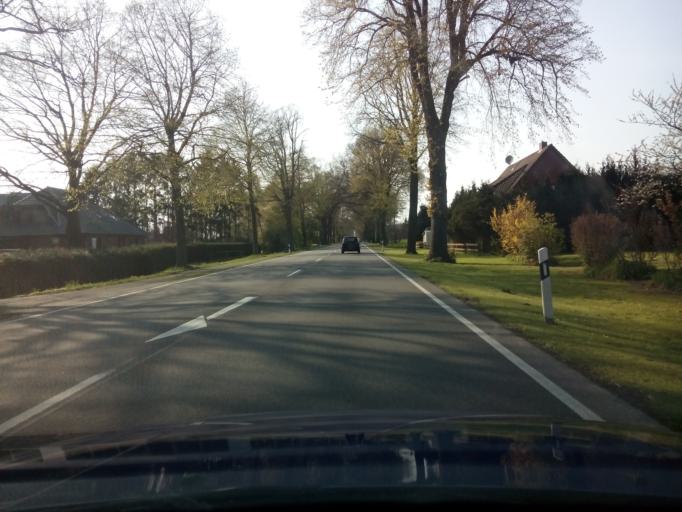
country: DE
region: Lower Saxony
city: Bruchhausen-Vilsen
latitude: 52.8144
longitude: 8.9563
